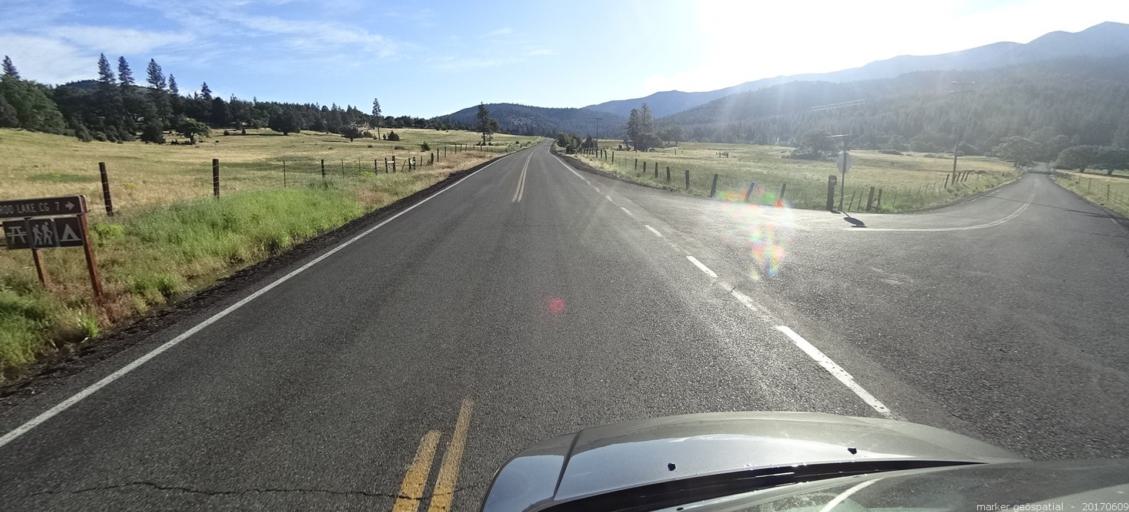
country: US
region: California
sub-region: Siskiyou County
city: Weed
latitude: 41.3870
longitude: -122.6800
